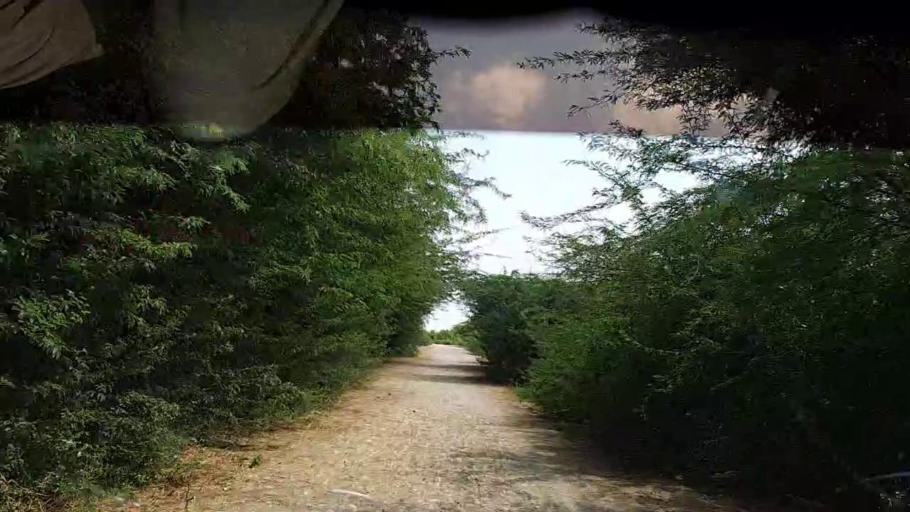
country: PK
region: Sindh
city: Kadhan
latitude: 24.5996
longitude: 68.9879
